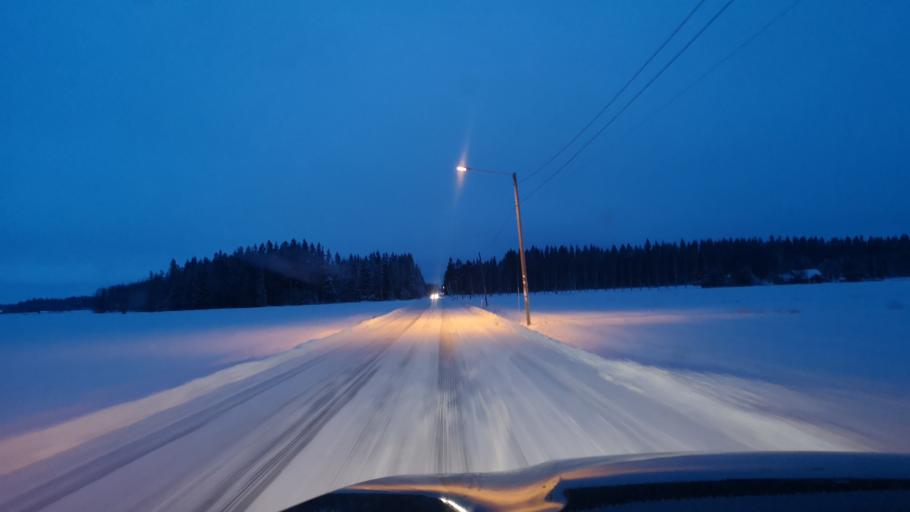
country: FI
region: Varsinais-Suomi
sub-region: Loimaa
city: Loimaa
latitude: 60.8742
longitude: 23.0898
